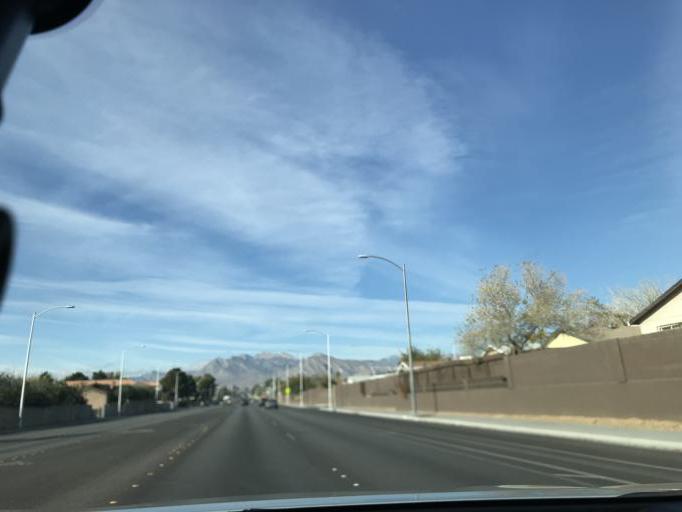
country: US
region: Nevada
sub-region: Clark County
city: Spring Valley
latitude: 36.2032
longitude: -115.2298
